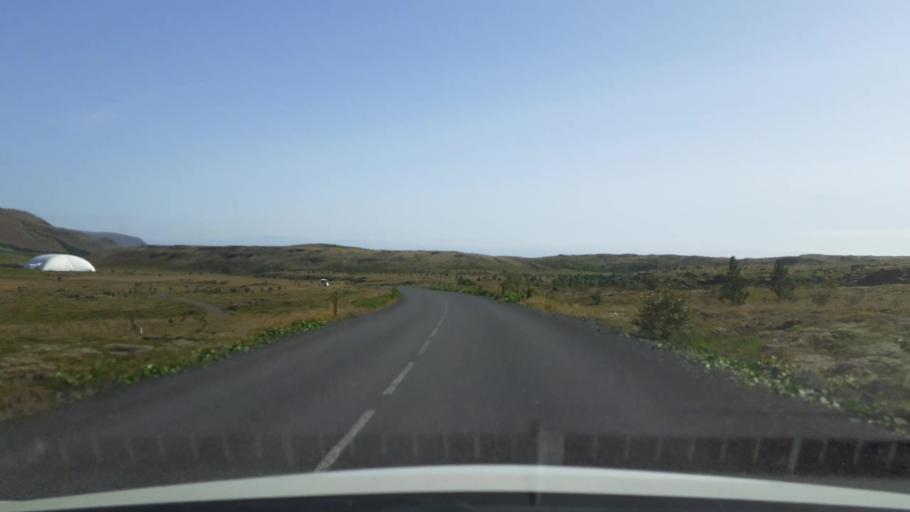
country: IS
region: South
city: Hveragerdi
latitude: 64.0156
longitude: -21.2102
